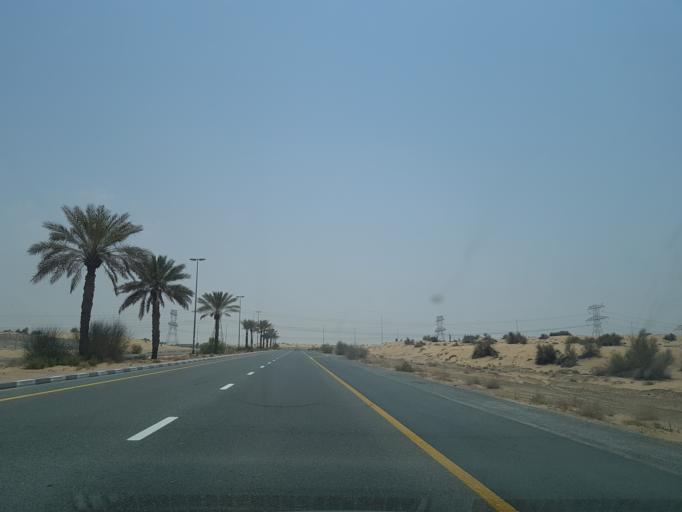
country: AE
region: Ash Shariqah
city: Sharjah
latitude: 25.1059
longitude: 55.4122
